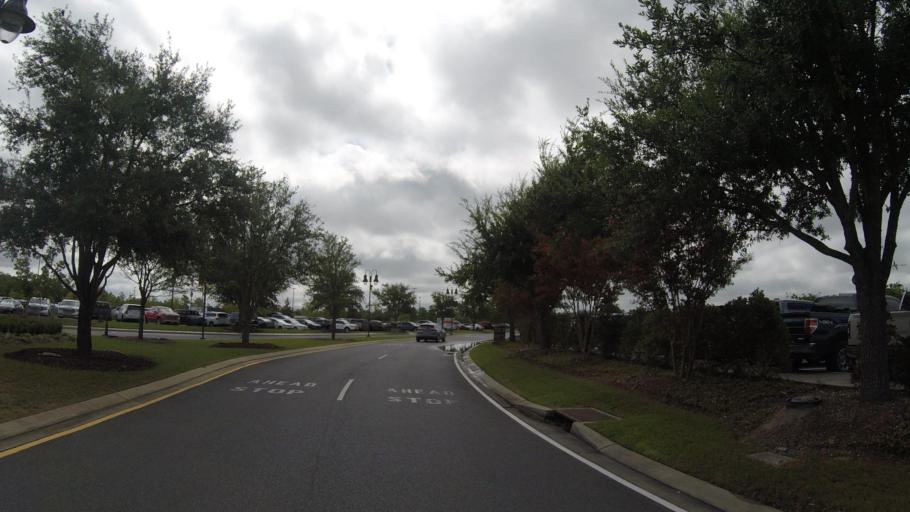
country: US
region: Louisiana
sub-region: Calcasieu Parish
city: Prien
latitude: 30.2037
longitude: -93.2633
